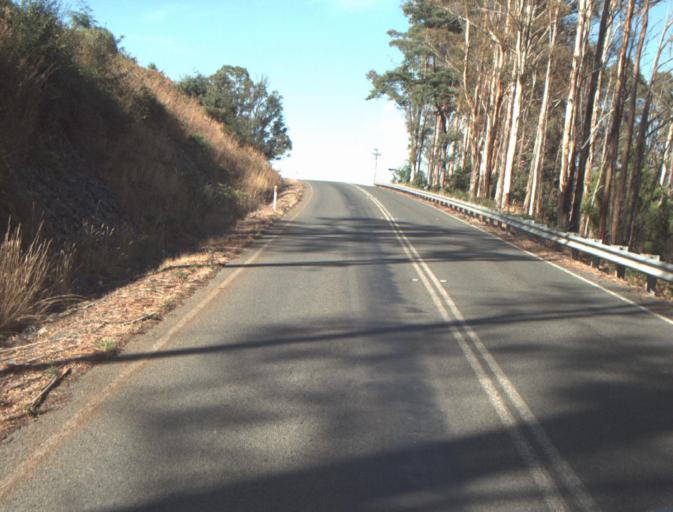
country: AU
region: Tasmania
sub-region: Dorset
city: Bridport
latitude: -41.1679
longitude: 147.2315
